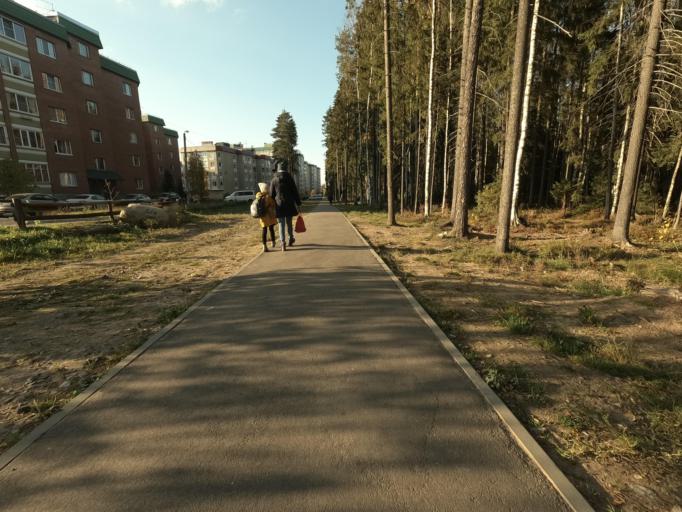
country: RU
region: Leningrad
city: Sertolovo
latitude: 60.1451
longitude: 30.2284
